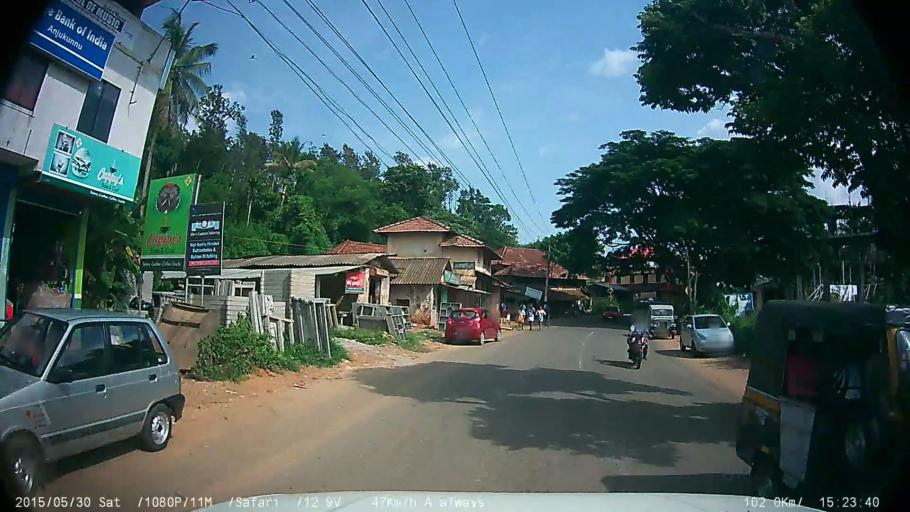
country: IN
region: Kerala
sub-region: Wayanad
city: Panamaram
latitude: 11.7358
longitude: 76.0732
